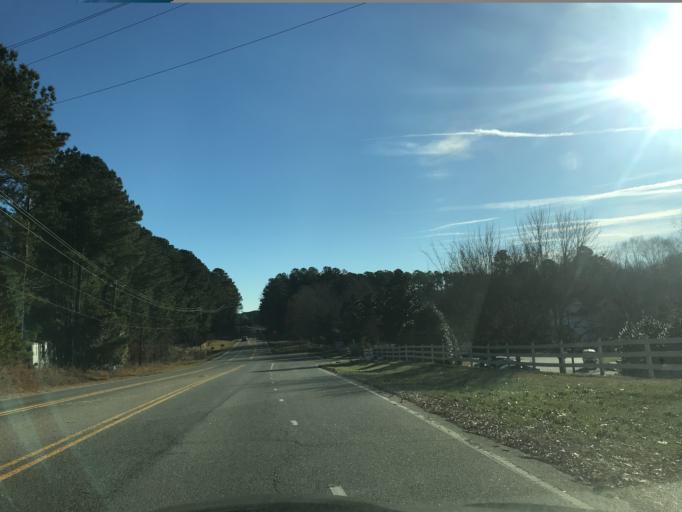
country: US
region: North Carolina
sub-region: Wake County
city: West Raleigh
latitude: 35.9063
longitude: -78.7019
